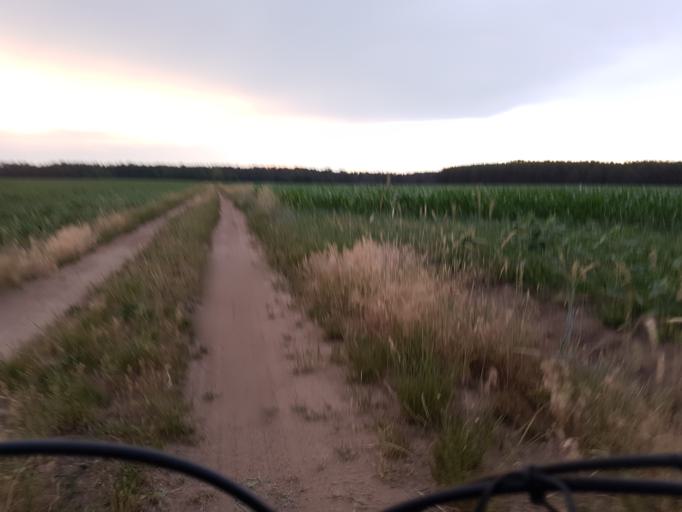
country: DE
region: Brandenburg
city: Schilda
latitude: 51.5781
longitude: 13.3547
